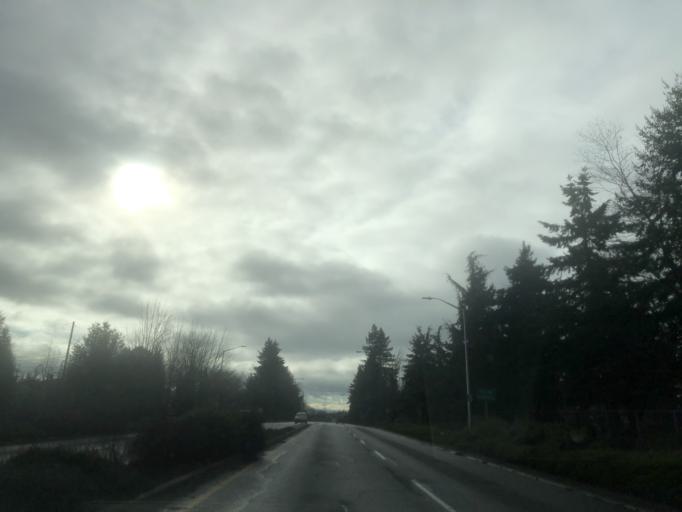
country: US
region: Washington
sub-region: Pierce County
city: Tacoma
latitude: 47.2401
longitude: -122.4632
